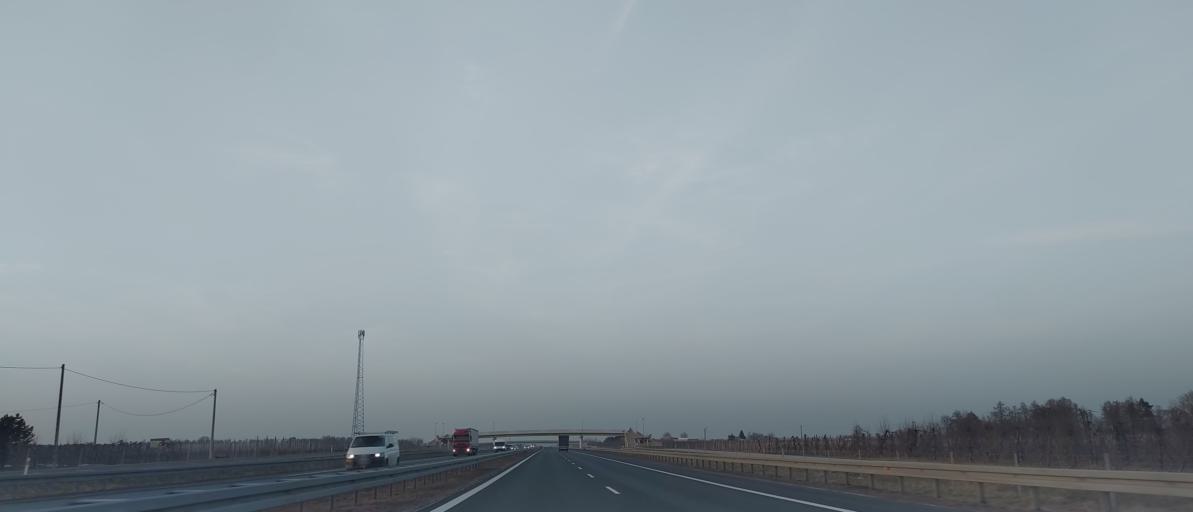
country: PL
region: Masovian Voivodeship
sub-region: Powiat grojecki
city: Jasieniec
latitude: 51.7779
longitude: 20.8969
